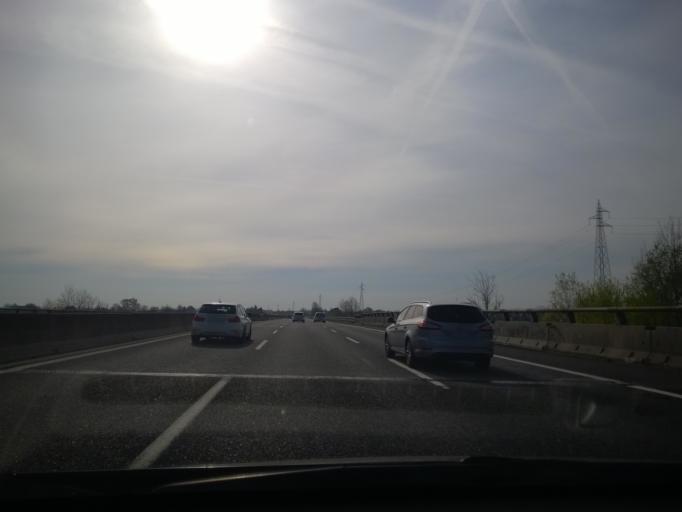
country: IT
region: Emilia-Romagna
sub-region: Forli-Cesena
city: Forli
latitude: 44.2865
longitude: 11.9985
